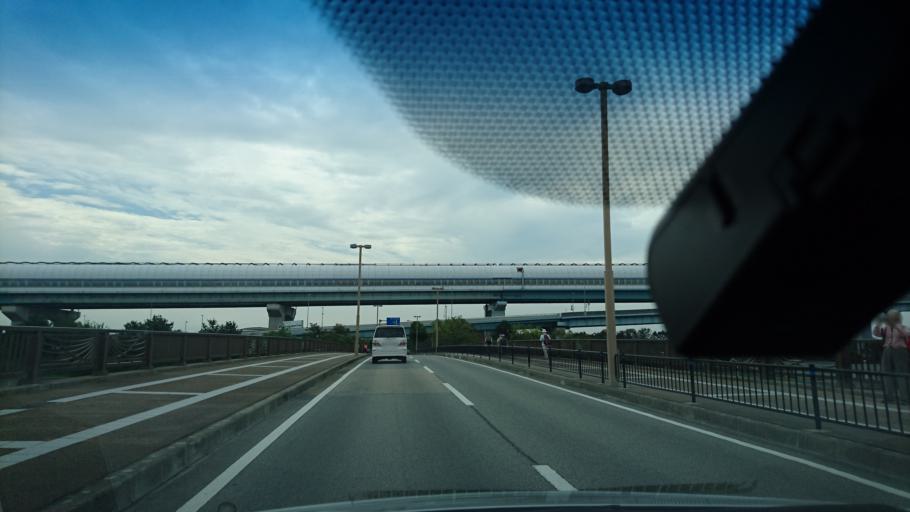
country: JP
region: Hyogo
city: Ashiya
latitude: 34.7148
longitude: 135.3089
